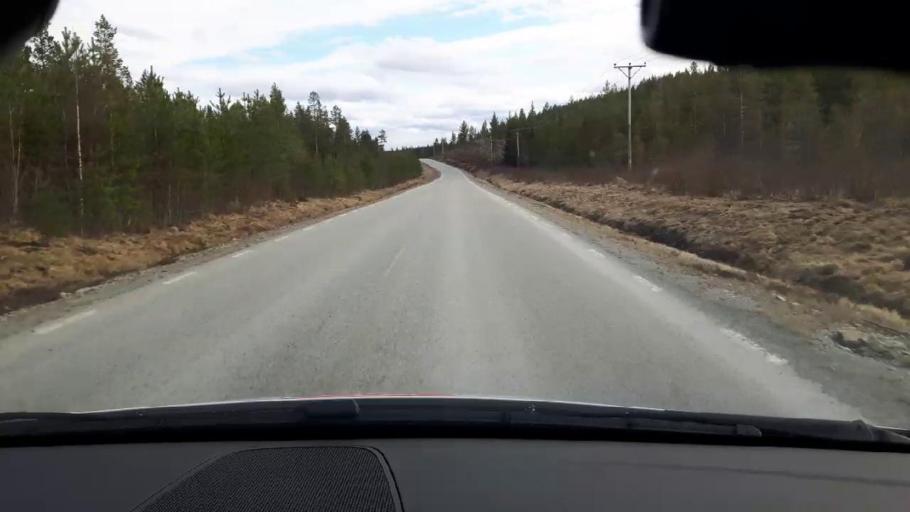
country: SE
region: Jaemtland
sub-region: Bergs Kommun
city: Hoverberg
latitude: 62.7146
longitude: 14.6083
